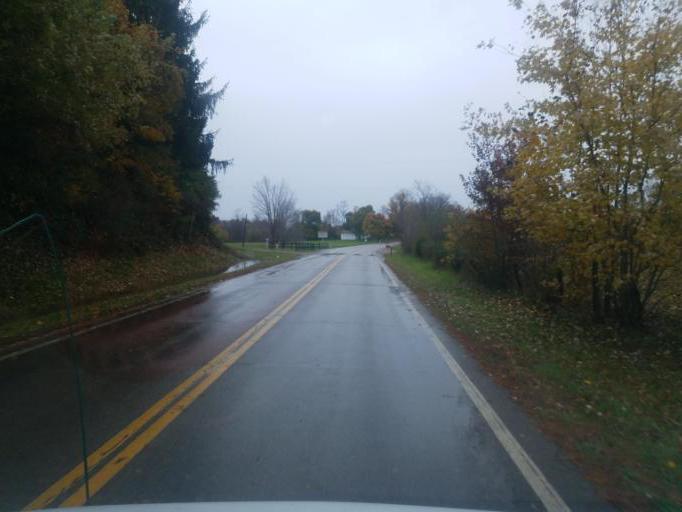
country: US
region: Ohio
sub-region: Morgan County
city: McConnelsville
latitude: 39.4837
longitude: -81.8684
